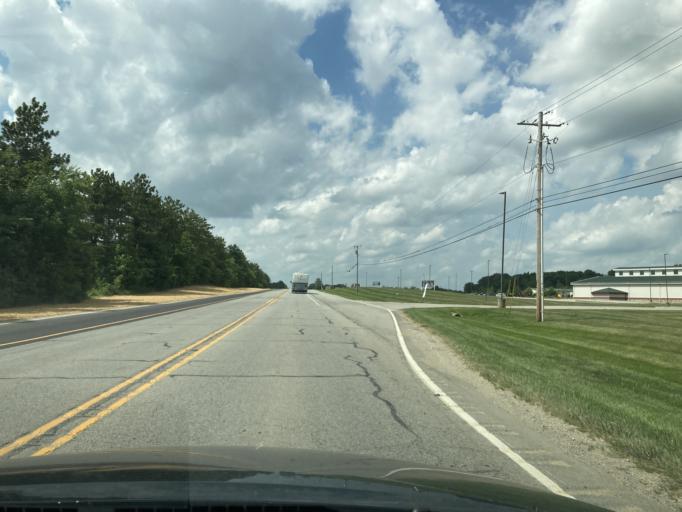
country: US
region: Indiana
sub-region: Boone County
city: Zionsville
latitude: 39.9841
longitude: -86.2577
